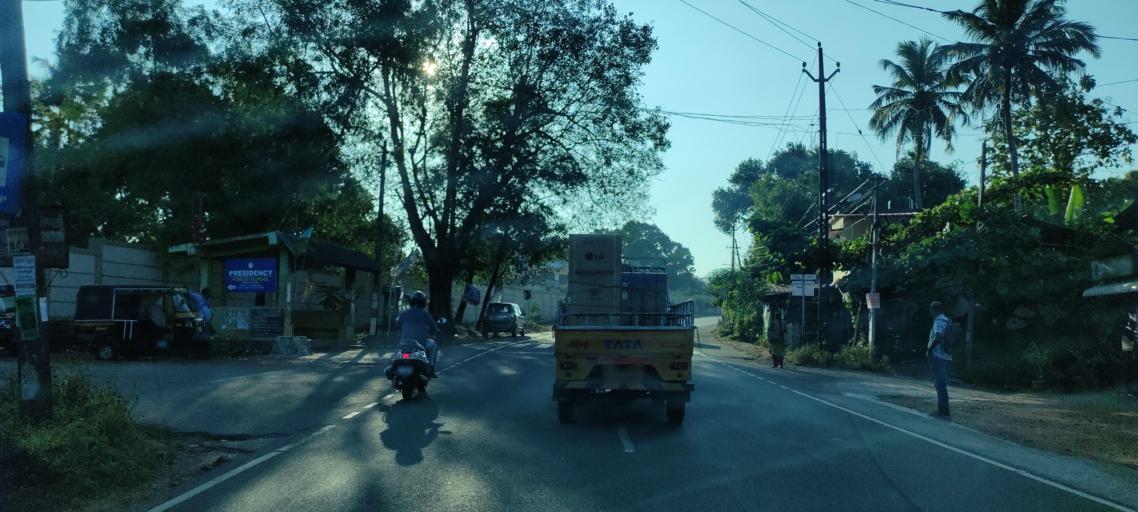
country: IN
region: Kerala
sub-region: Alappuzha
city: Kattanam
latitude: 9.1747
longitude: 76.6299
